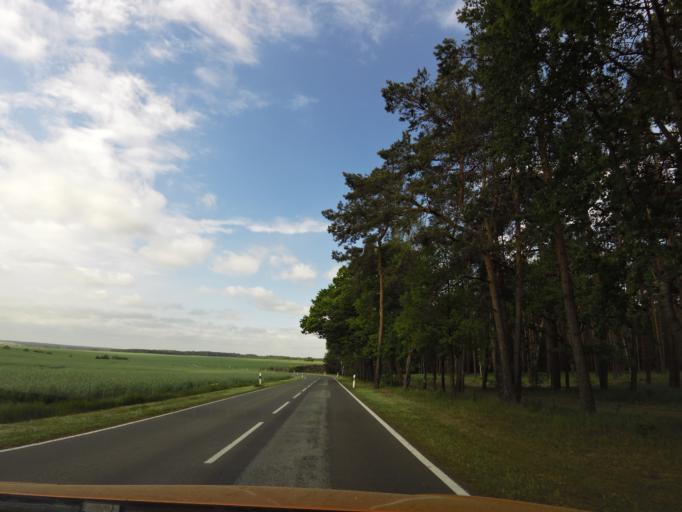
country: DE
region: Brandenburg
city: Belzig
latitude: 52.0932
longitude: 12.5462
